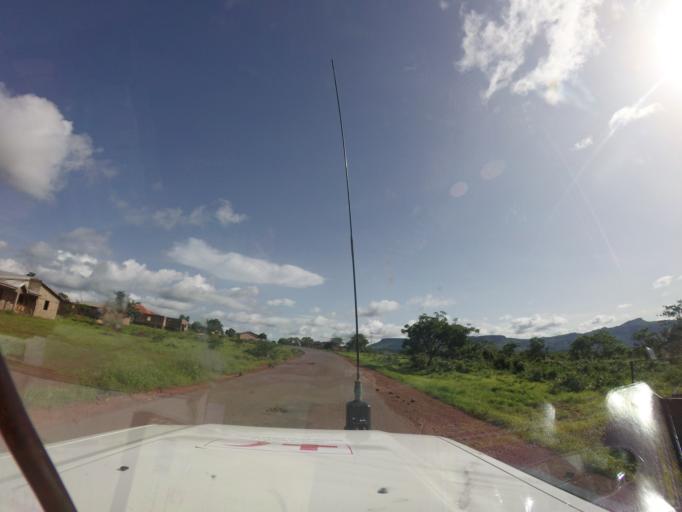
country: GN
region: Mamou
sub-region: Mamou Prefecture
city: Mamou
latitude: 10.2693
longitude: -12.4525
